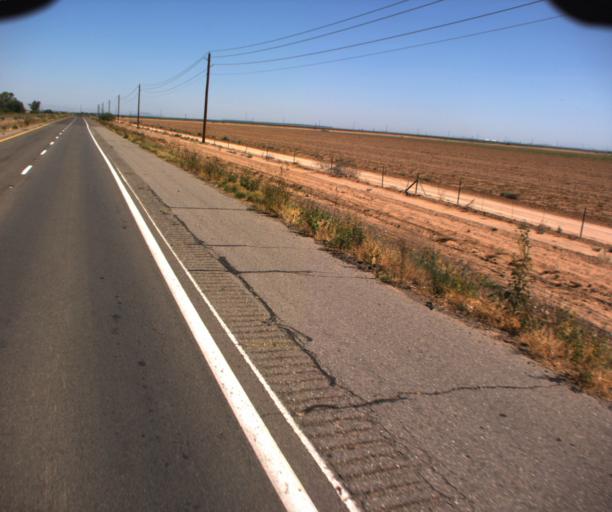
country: US
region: Arizona
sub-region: Pinal County
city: Maricopa
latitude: 32.9323
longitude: -112.0493
